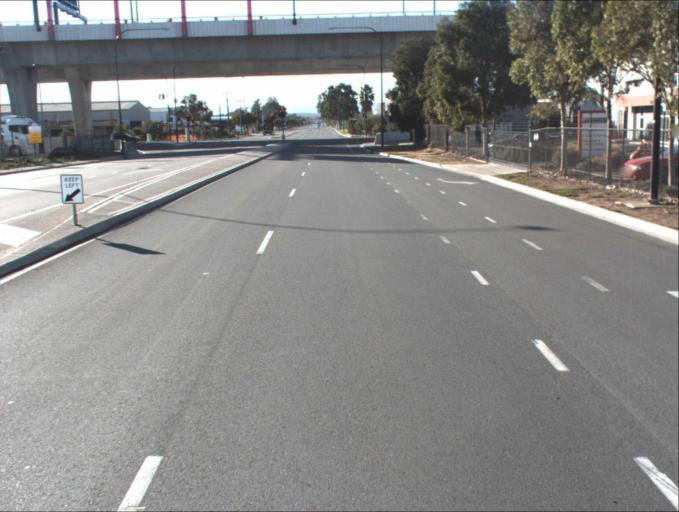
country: AU
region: South Australia
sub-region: Port Adelaide Enfield
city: Blair Athol
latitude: -34.8406
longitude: 138.5640
